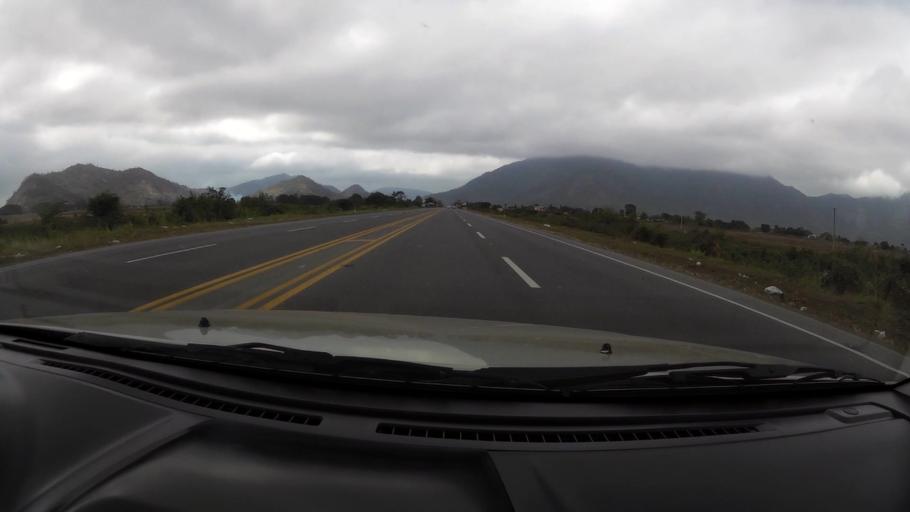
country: EC
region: Guayas
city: Coronel Marcelino Mariduena
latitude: -2.3694
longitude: -79.6323
